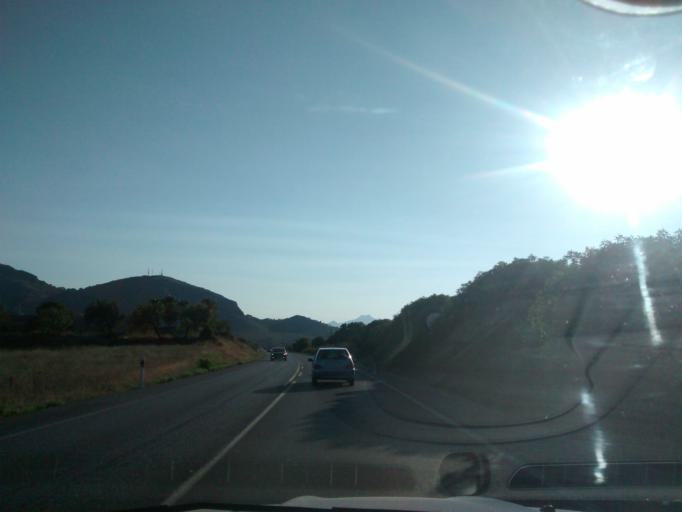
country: ES
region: Balearic Islands
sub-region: Illes Balears
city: Alcudia
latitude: 39.8457
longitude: 3.1199
